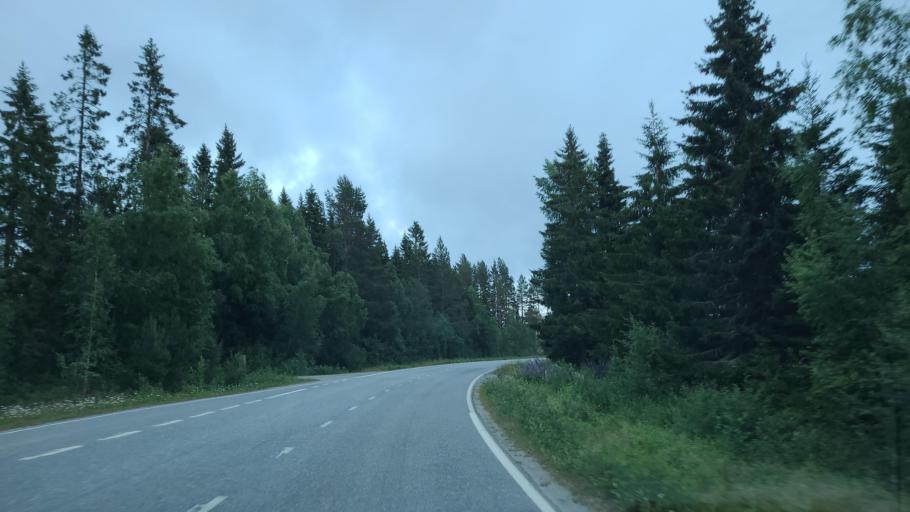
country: FI
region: Ostrobothnia
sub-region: Vaasa
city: Replot
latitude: 63.2799
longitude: 21.1328
